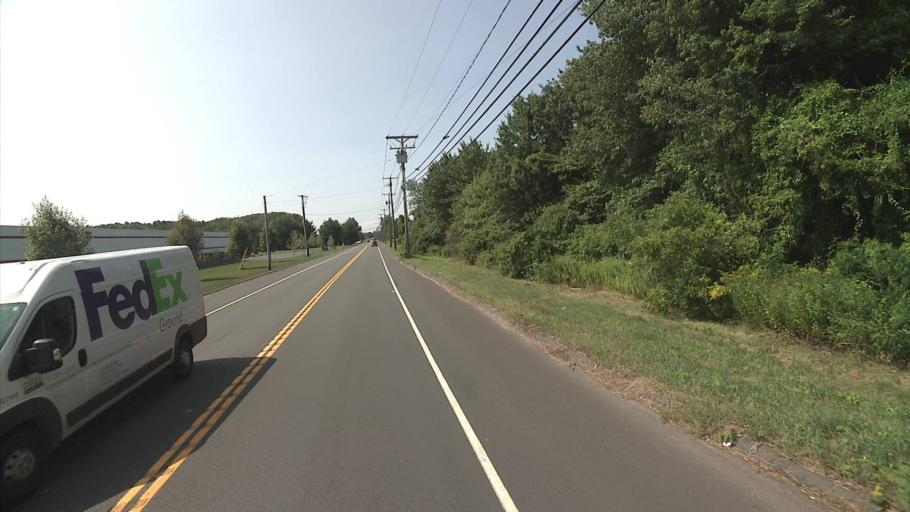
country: US
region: Connecticut
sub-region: Hartford County
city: South Windsor
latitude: 41.8535
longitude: -72.5872
